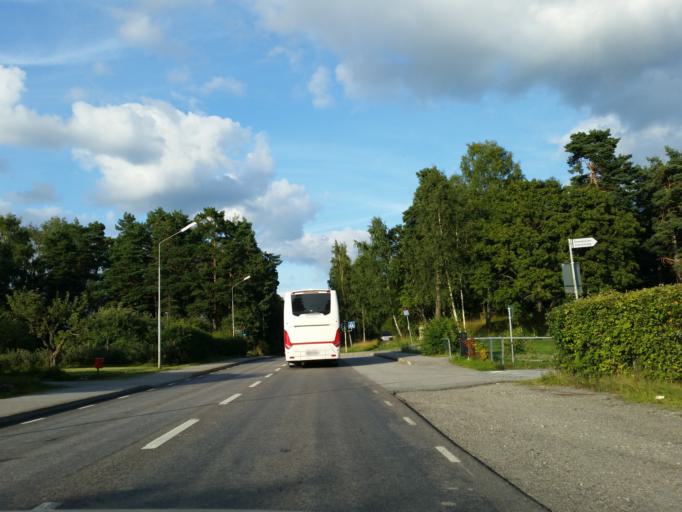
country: SE
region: Stockholm
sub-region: Sodertalje Kommun
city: Pershagen
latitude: 59.0844
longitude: 17.5569
